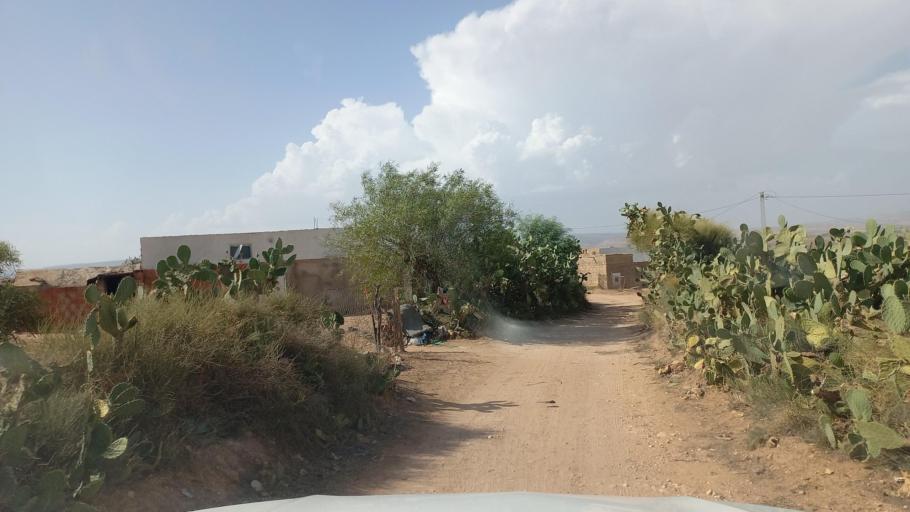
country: TN
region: Al Qasrayn
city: Kasserine
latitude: 35.2097
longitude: 8.9821
